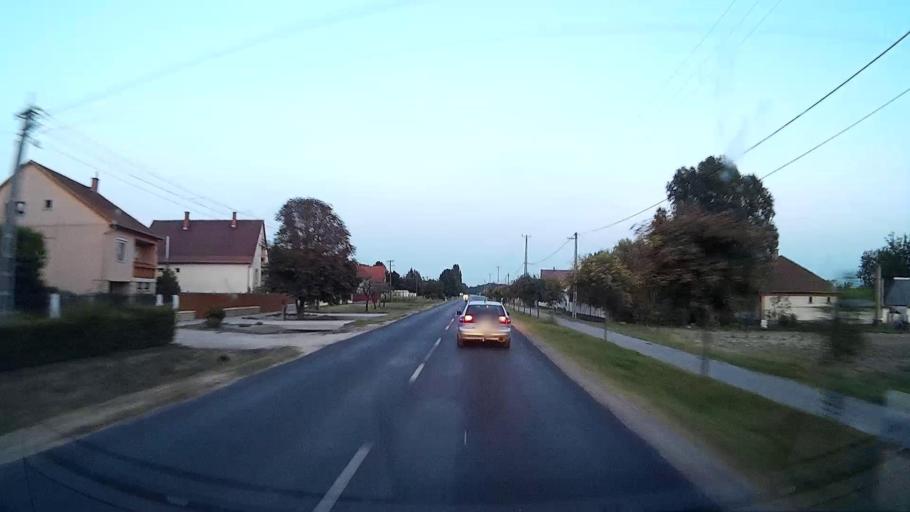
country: HU
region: Pest
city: Cegledbercel
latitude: 47.2104
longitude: 19.6830
